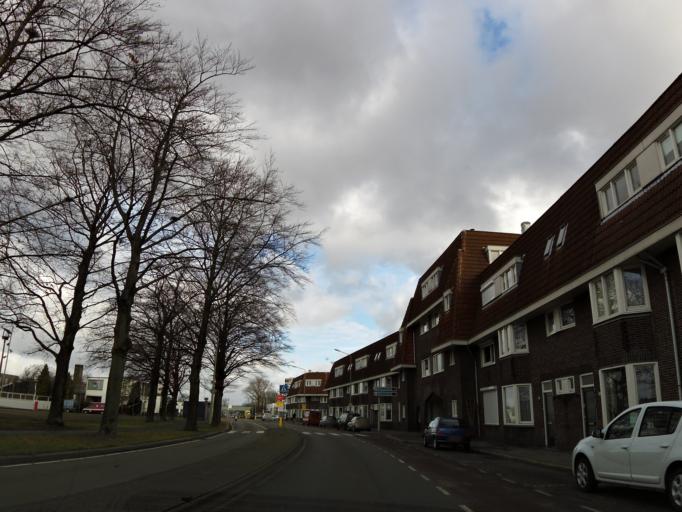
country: NL
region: Limburg
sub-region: Gemeente Maastricht
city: Maastricht
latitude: 50.8554
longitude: 5.6993
